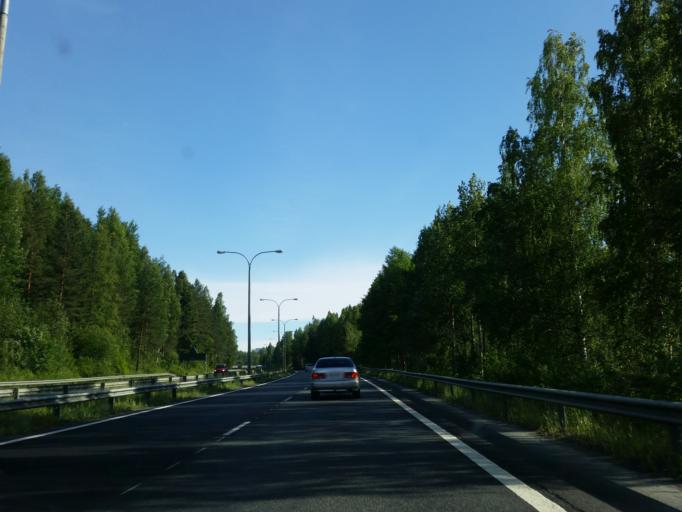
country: FI
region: Northern Savo
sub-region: Kuopio
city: Kuopio
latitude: 62.9258
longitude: 27.6753
